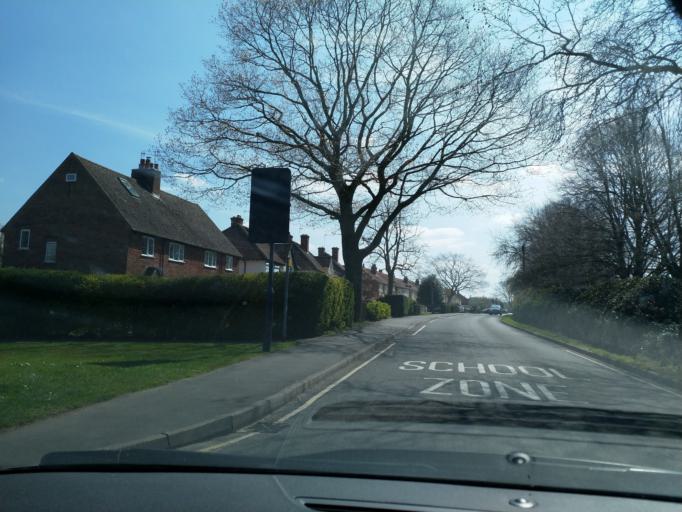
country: GB
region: England
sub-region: Warwickshire
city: Stratford-upon-Avon
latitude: 52.1980
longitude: -1.6774
